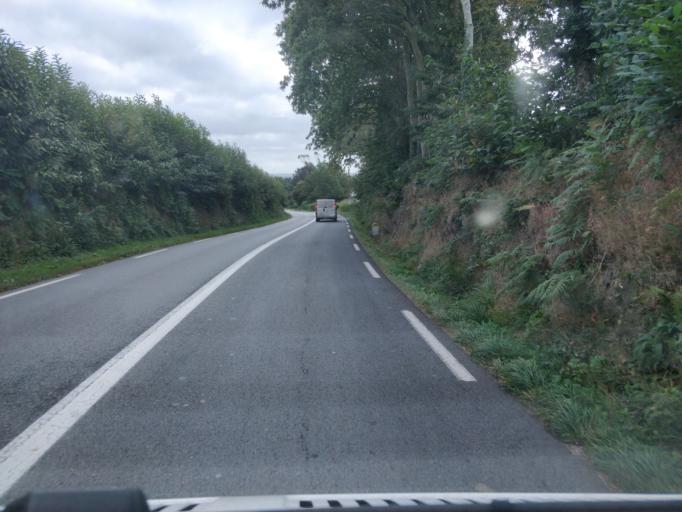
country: FR
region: Brittany
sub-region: Departement du Finistere
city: Pluguffan
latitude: 48.0000
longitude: -4.1696
